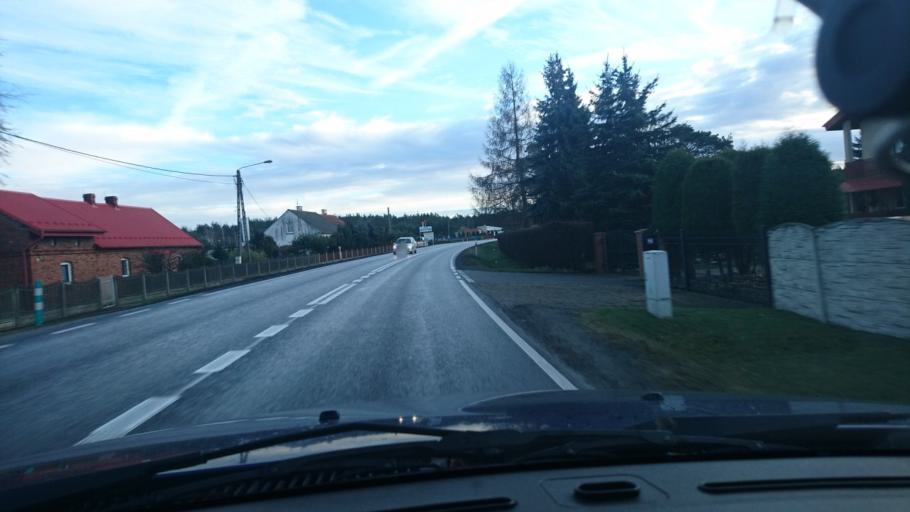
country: PL
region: Greater Poland Voivodeship
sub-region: Powiat kepinski
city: Bralin
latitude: 51.3494
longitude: 17.9494
